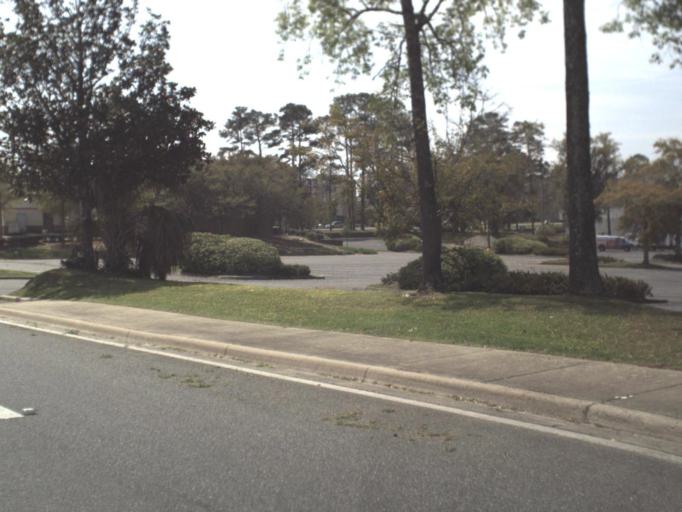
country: US
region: Florida
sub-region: Leon County
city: Tallahassee
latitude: 30.4288
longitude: -84.2269
